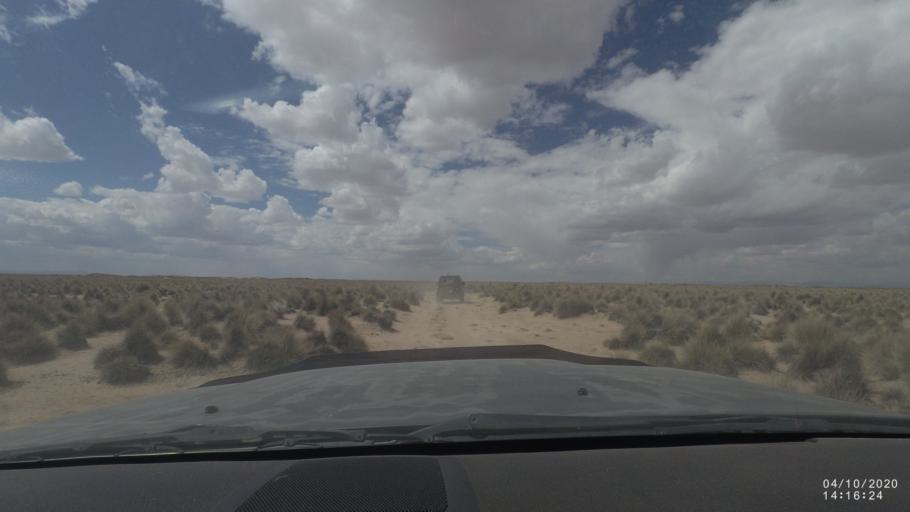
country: BO
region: Oruro
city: Poopo
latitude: -18.6906
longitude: -67.4527
